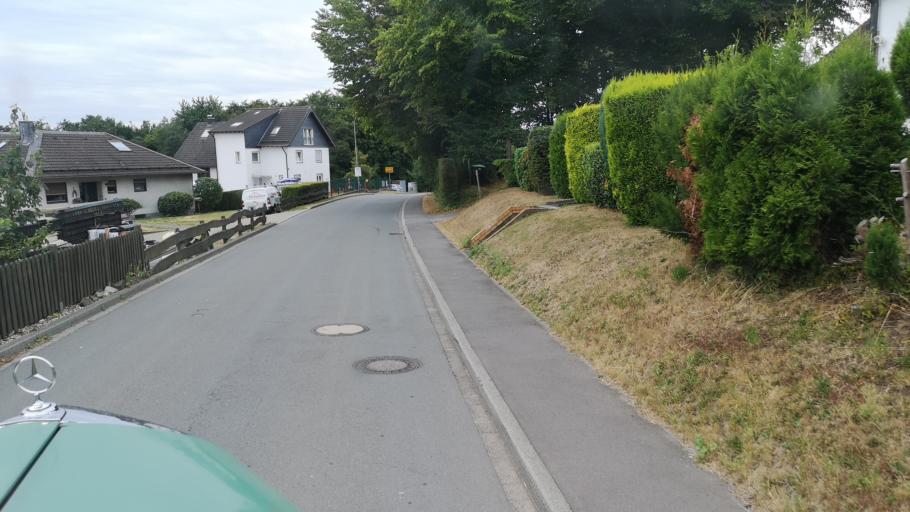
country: DE
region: North Rhine-Westphalia
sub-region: Regierungsbezirk Koln
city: Odenthal
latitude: 51.0591
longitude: 7.1515
